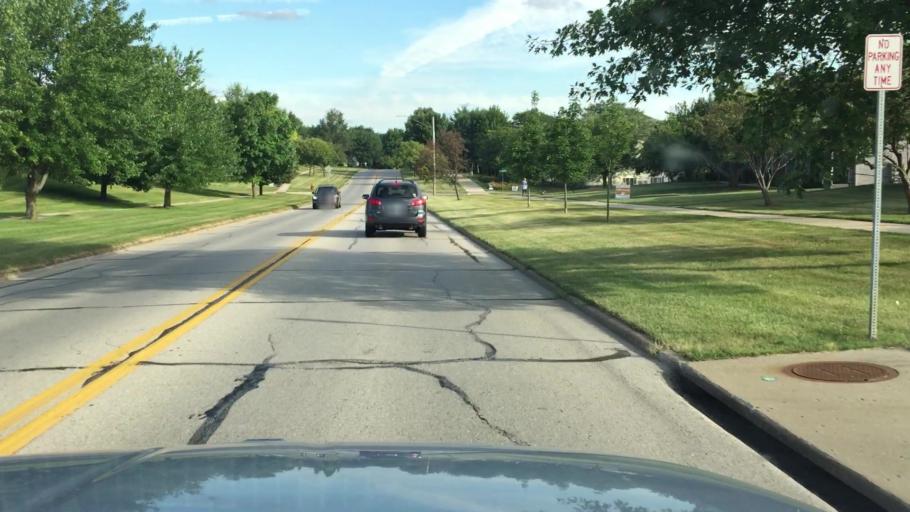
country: US
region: Iowa
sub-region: Johnson County
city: Iowa City
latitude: 41.6612
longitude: -91.4825
